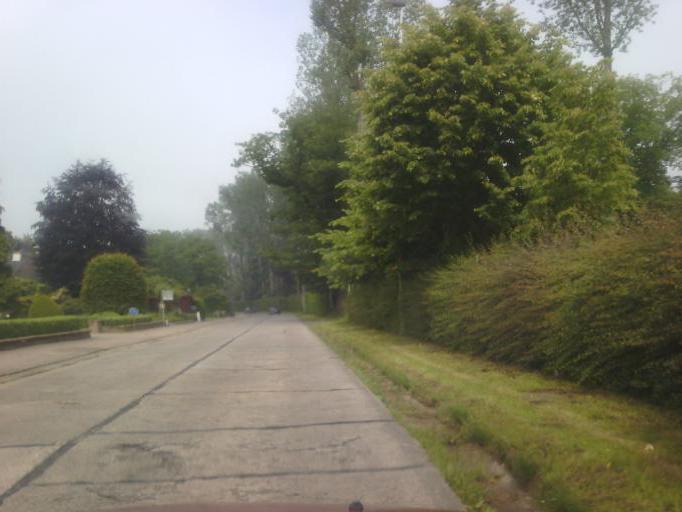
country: BE
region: Flanders
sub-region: Provincie Oost-Vlaanderen
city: Aalst
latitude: 50.9894
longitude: 4.0399
